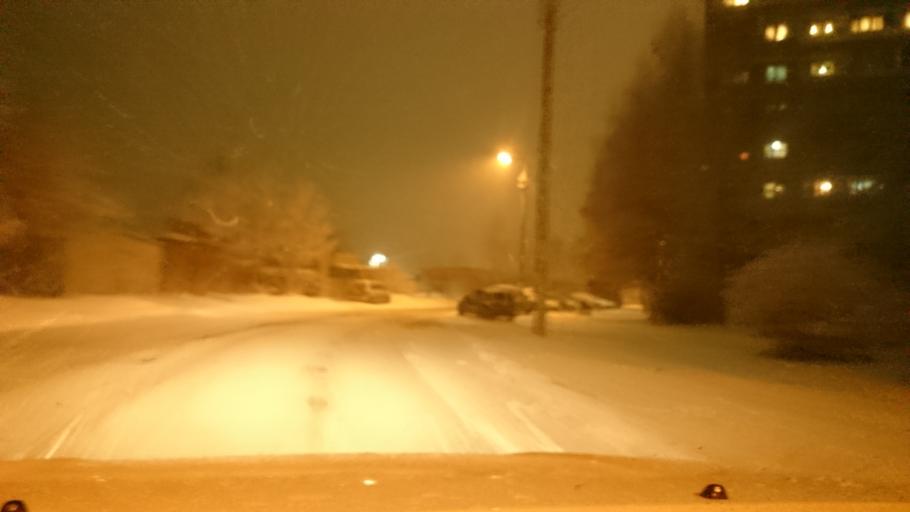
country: RU
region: Tula
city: Mendeleyevskiy
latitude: 54.1647
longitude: 37.5613
